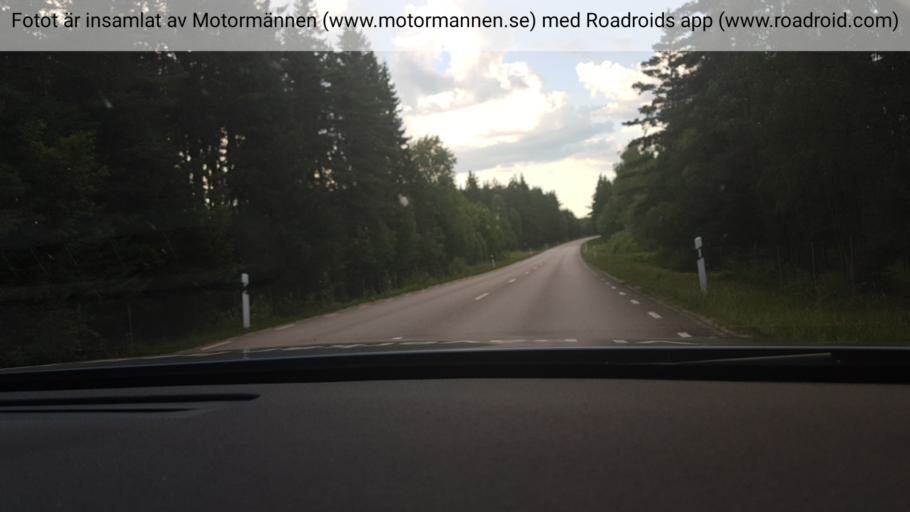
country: SE
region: Vaestra Goetaland
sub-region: Tidaholms Kommun
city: Tidaholm
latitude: 58.1301
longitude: 13.8951
